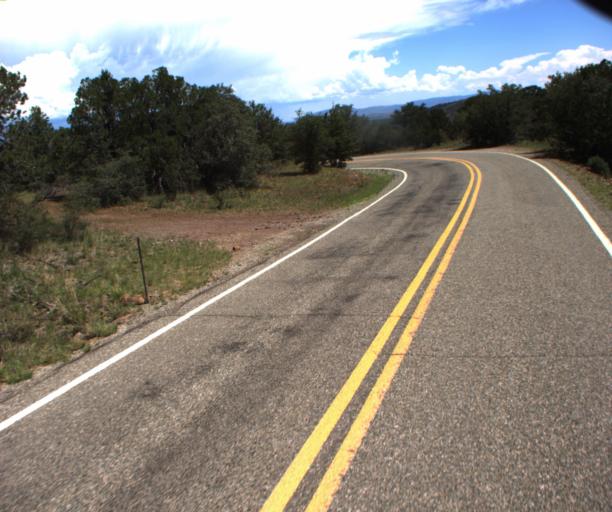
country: US
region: Arizona
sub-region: Greenlee County
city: Morenci
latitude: 33.2571
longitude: -109.3686
